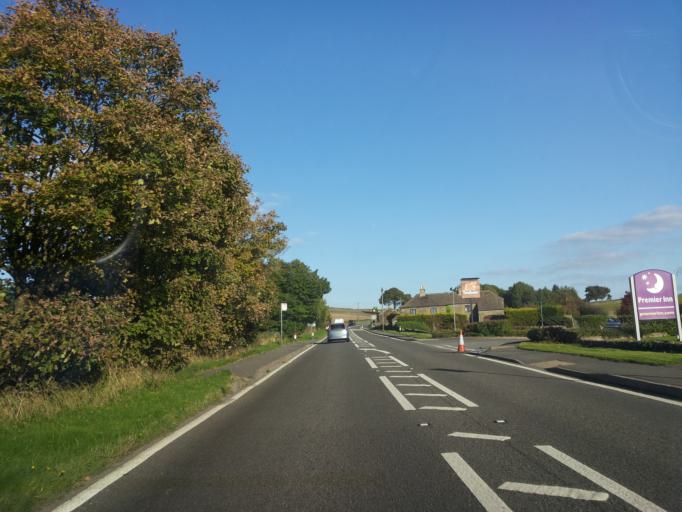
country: GB
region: England
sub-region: Derbyshire
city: Dronfield
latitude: 53.2382
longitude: -1.5435
